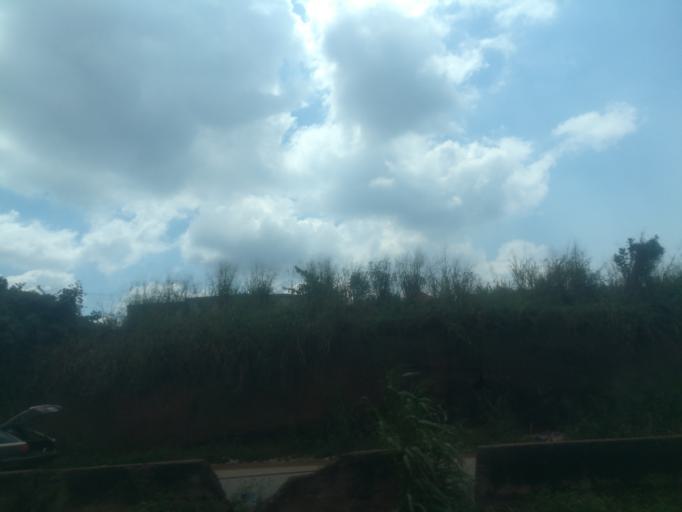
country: NG
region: Oyo
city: Ibadan
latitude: 7.3905
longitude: 3.9760
